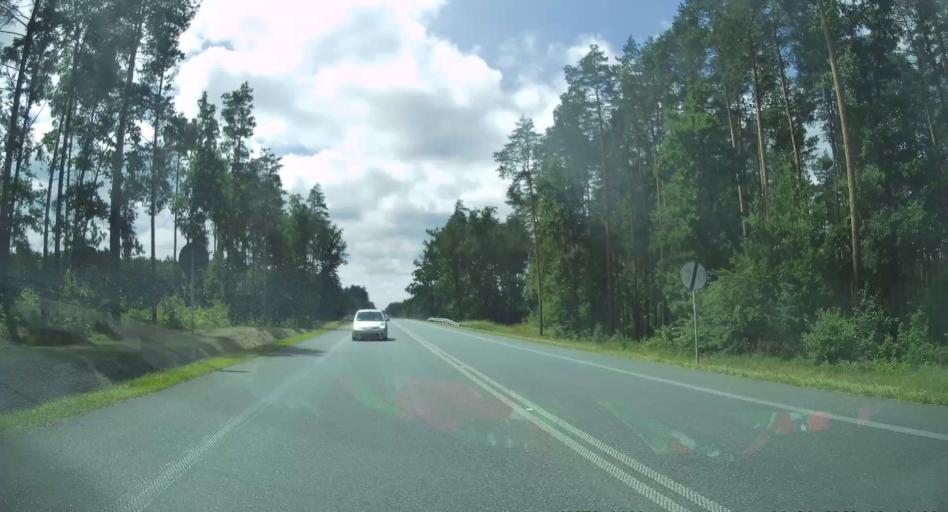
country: PL
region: Subcarpathian Voivodeship
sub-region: Powiat mielecki
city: Mielec
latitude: 50.3123
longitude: 21.5036
